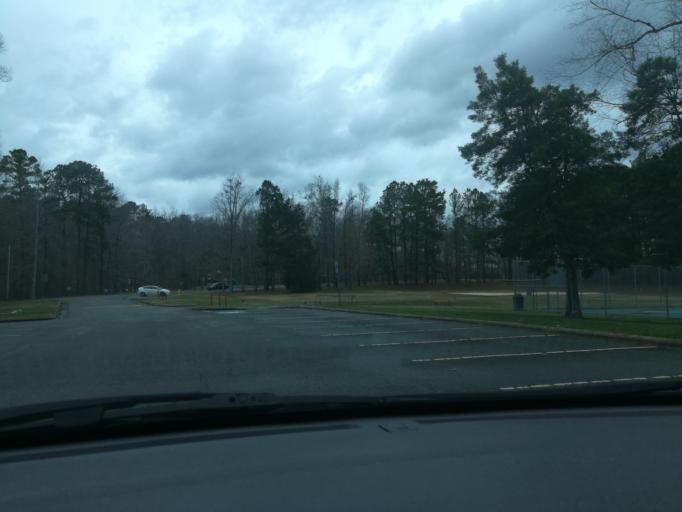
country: US
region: North Carolina
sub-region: Orange County
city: Carrboro
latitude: 35.9224
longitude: -79.1056
